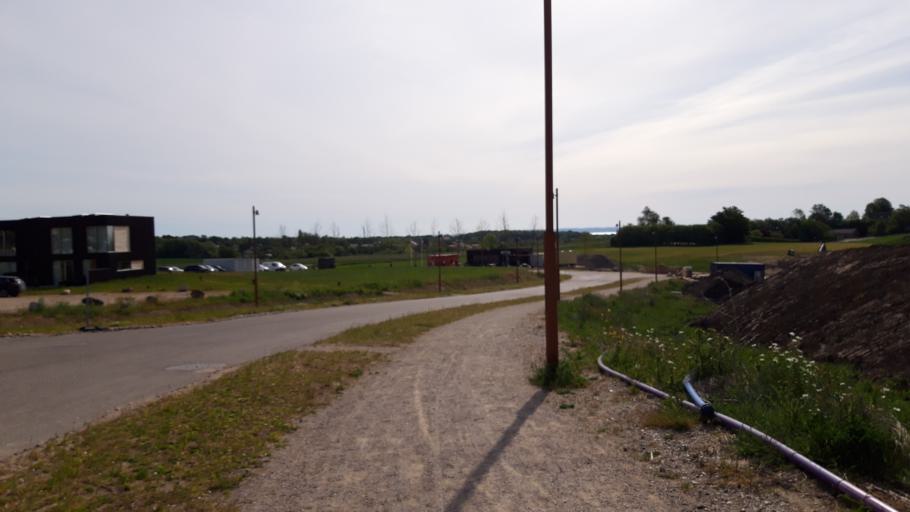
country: DK
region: Central Jutland
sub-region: Arhus Kommune
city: Lystrup
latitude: 56.2338
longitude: 10.2043
